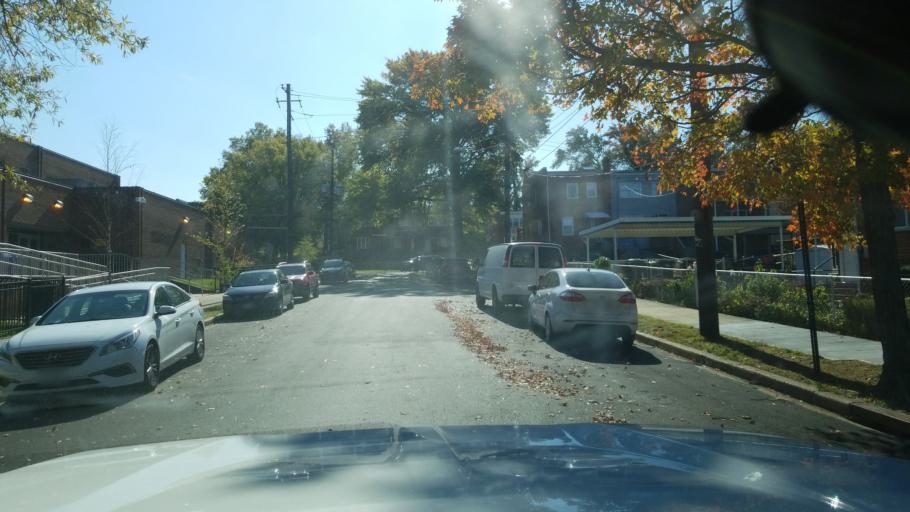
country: US
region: Maryland
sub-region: Prince George's County
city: Chillum
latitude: 38.9502
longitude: -76.9868
